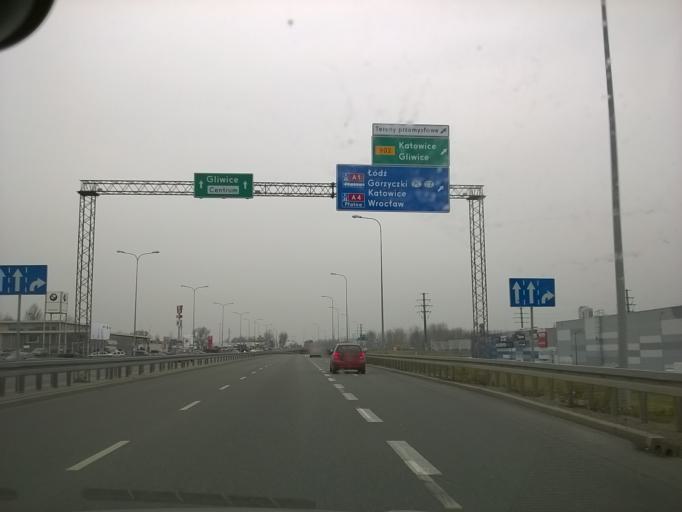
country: PL
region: Silesian Voivodeship
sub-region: Powiat gliwicki
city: Przyszowice
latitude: 50.2653
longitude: 18.7165
